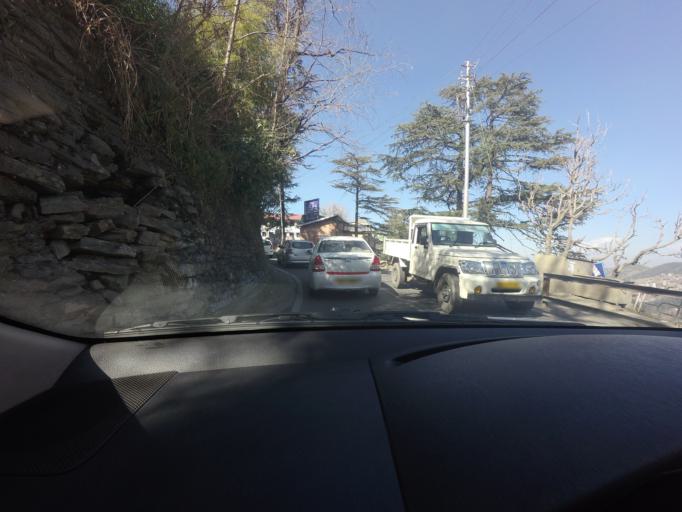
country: IN
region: Himachal Pradesh
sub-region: Shimla
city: Shimla
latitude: 31.1094
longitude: 77.1659
